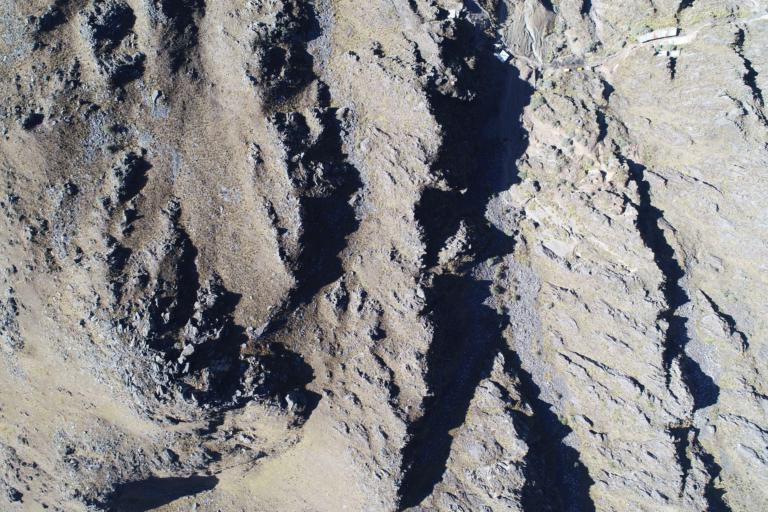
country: BO
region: La Paz
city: Sorata
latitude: -15.6546
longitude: -68.5321
